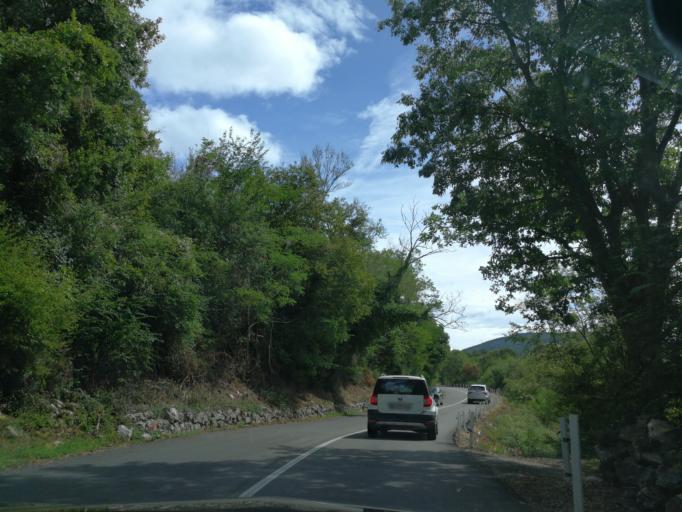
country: HR
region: Primorsko-Goranska
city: Punat
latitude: 45.0824
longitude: 14.6496
